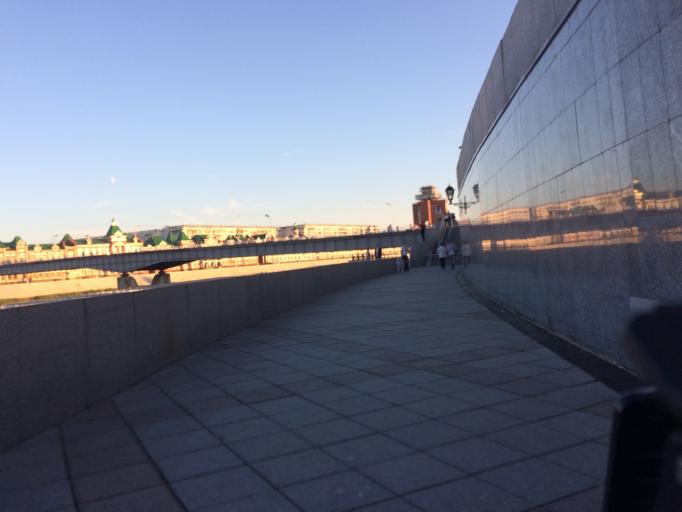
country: RU
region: Mariy-El
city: Yoshkar-Ola
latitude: 56.6339
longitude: 47.9055
